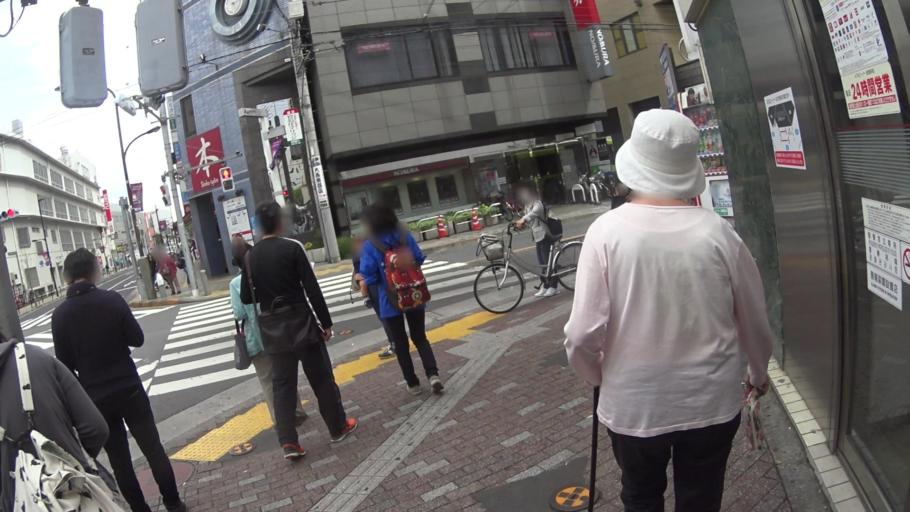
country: JP
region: Tokyo
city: Chofugaoka
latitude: 35.6502
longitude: 139.5447
